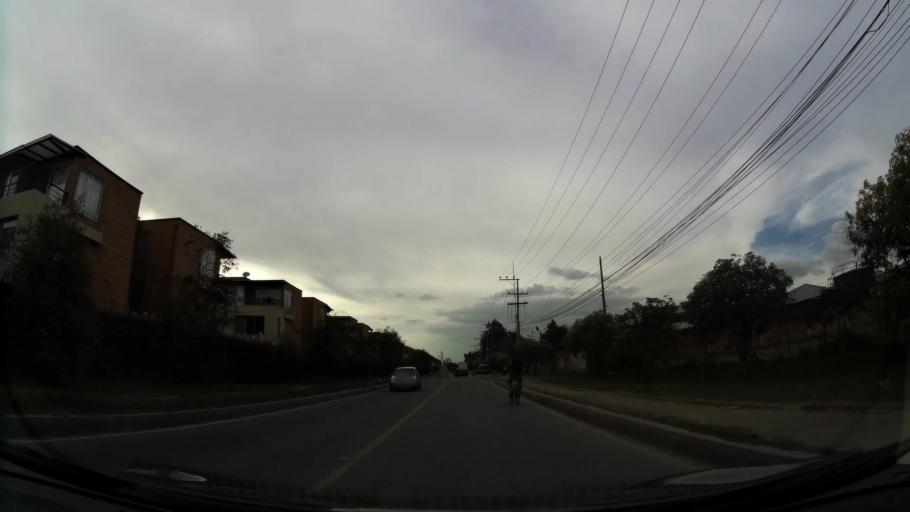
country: CO
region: Cundinamarca
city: Mosquera
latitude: 4.7080
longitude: -74.2332
